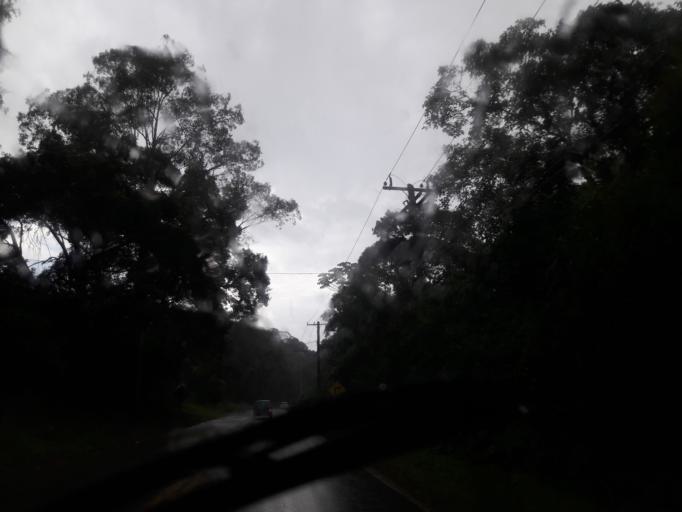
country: BR
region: Sao Paulo
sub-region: Bom Jesus Dos Perdoes
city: Bom Jesus dos Perdoes
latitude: -23.2705
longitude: -46.4195
